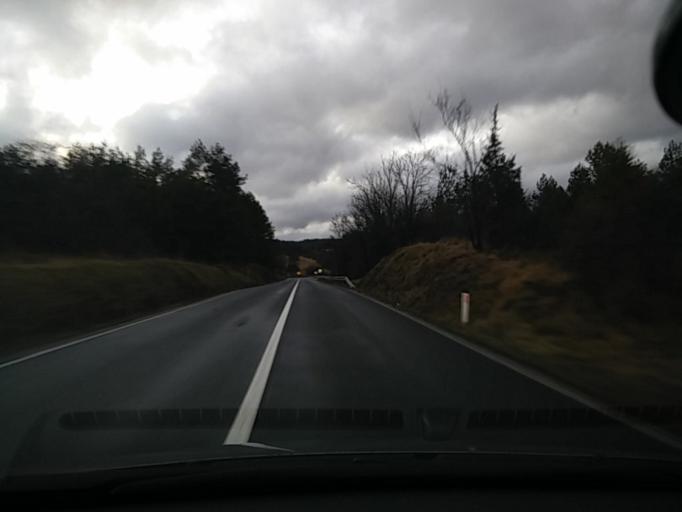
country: SI
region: Pivka
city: Pivka
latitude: 45.5283
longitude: 14.1283
